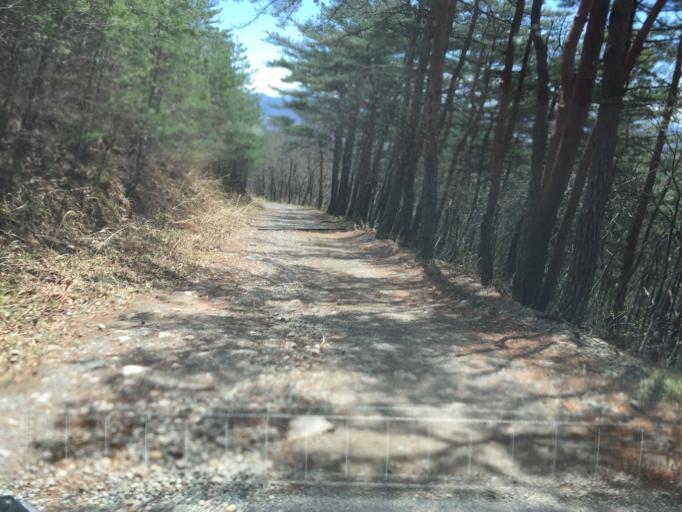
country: JP
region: Fukushima
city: Fukushima-shi
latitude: 37.8510
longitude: 140.4184
